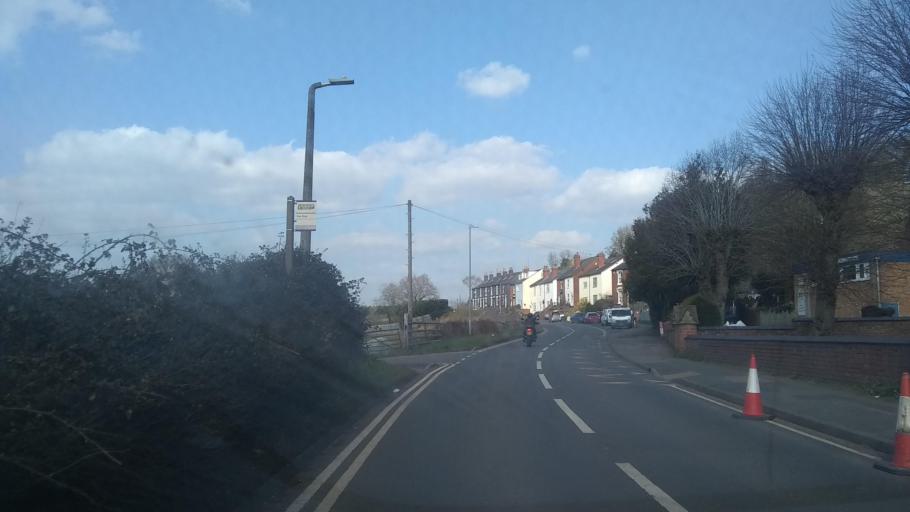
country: GB
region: England
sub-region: Worcestershire
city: Stourport-on-Severn
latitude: 52.3477
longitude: -2.2601
